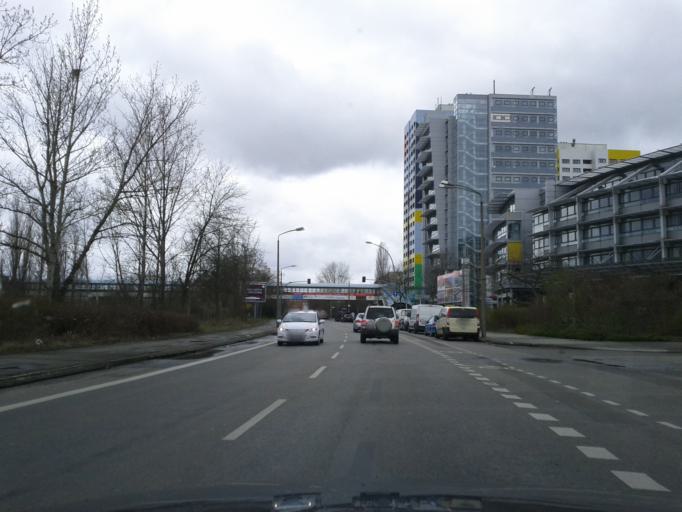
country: DE
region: Berlin
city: Fennpfuhl
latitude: 52.5240
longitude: 13.4671
